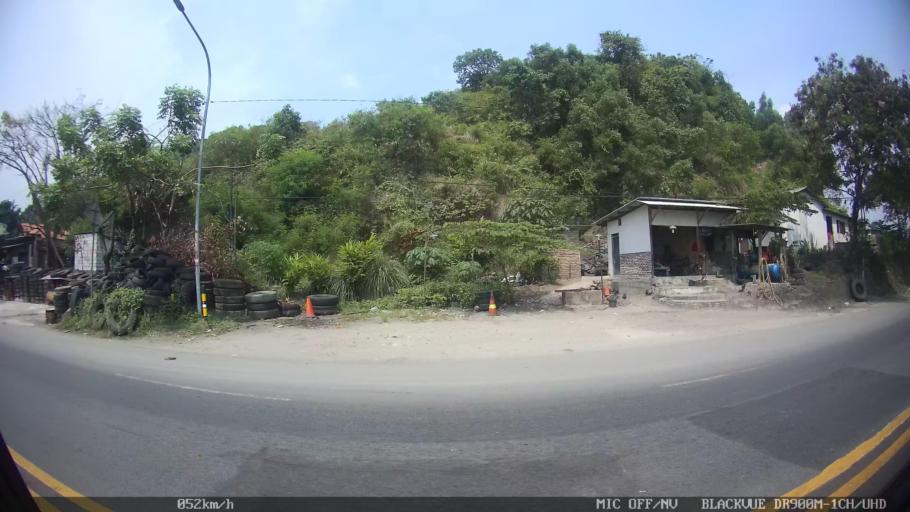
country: ID
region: Banten
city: Curug
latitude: -5.9527
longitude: 106.0018
